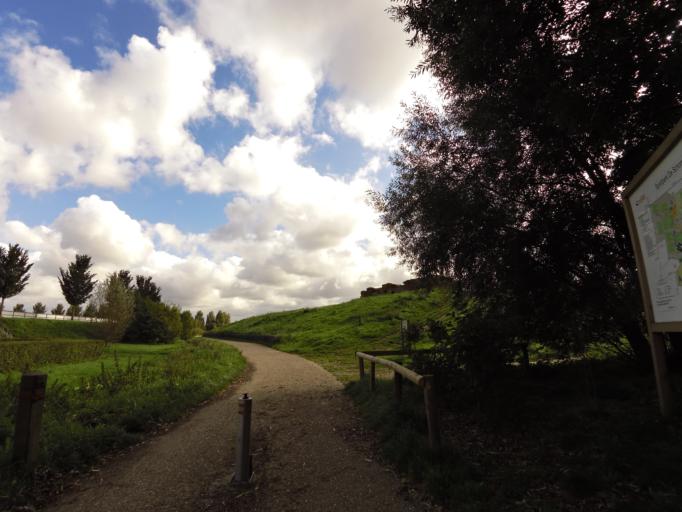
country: BE
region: Flanders
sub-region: Provincie West-Vlaanderen
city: Ostend
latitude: 51.1991
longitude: 2.9242
